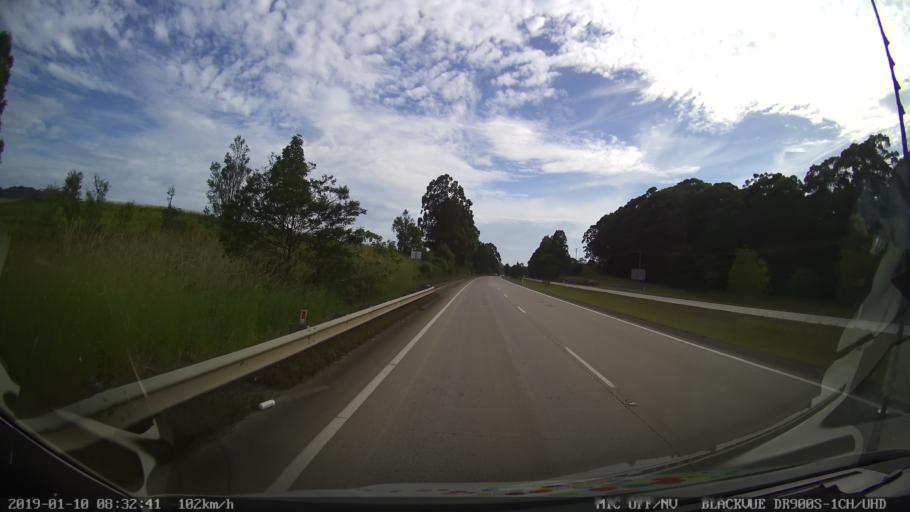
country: AU
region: New South Wales
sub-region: Coffs Harbour
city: Boambee
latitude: -30.3408
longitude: 153.0732
